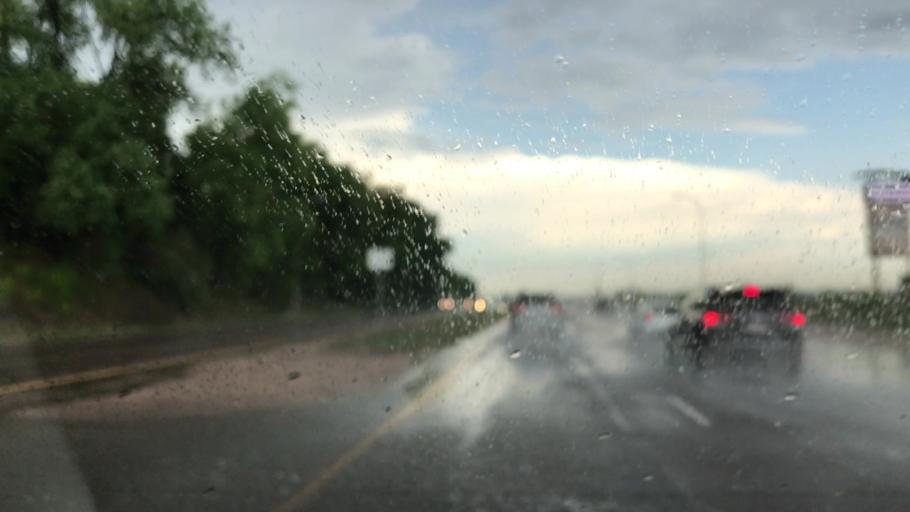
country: US
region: Colorado
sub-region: El Paso County
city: Colorado Springs
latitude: 38.8009
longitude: -104.8222
